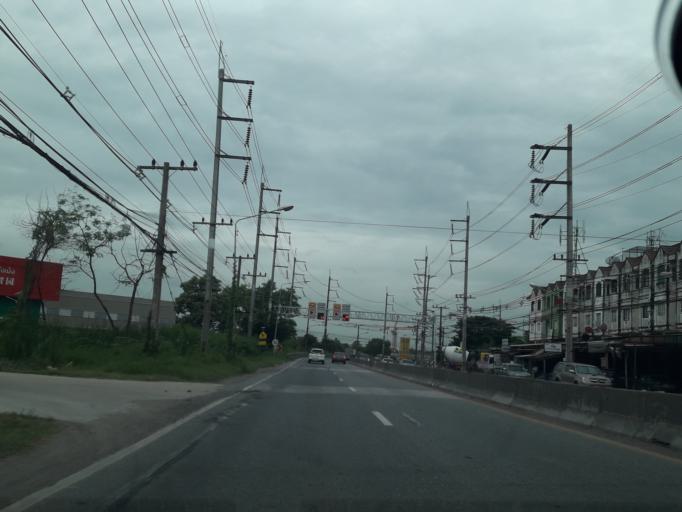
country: TH
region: Pathum Thani
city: Lam Luk Ka
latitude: 13.9419
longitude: 100.7678
